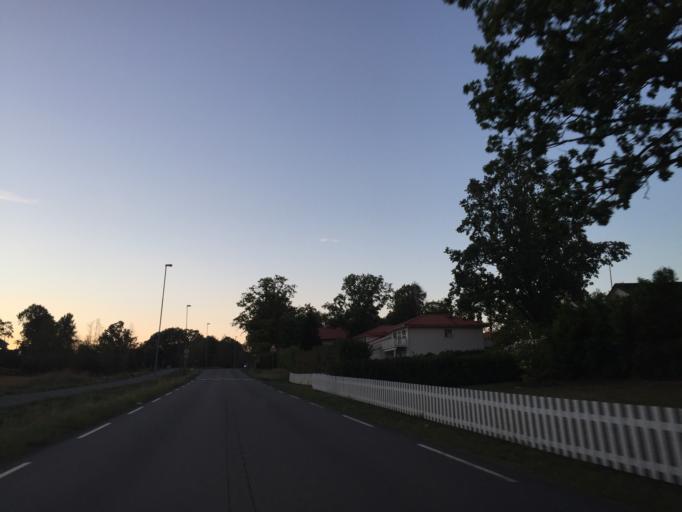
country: NO
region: Ostfold
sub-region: Moss
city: Moss
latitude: 59.4945
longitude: 10.6891
